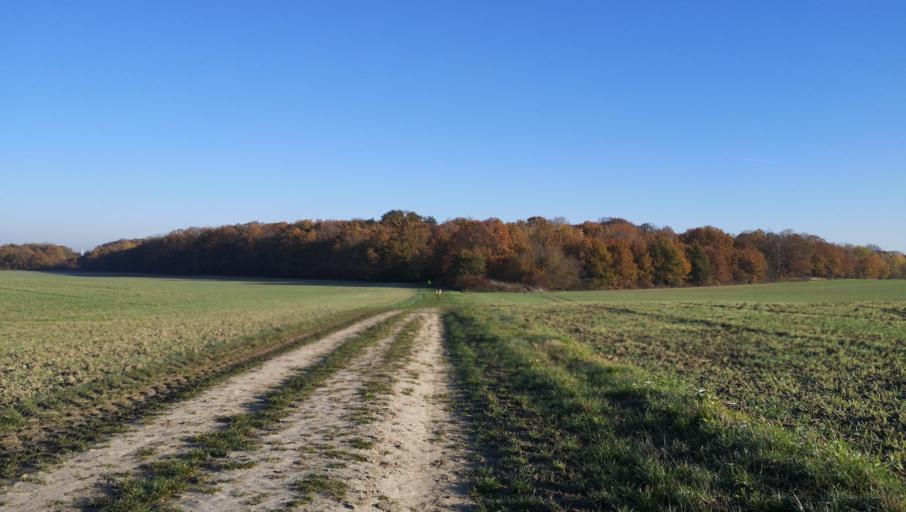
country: FR
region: Centre
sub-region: Departement du Loiret
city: Saran
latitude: 47.9404
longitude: 1.8574
